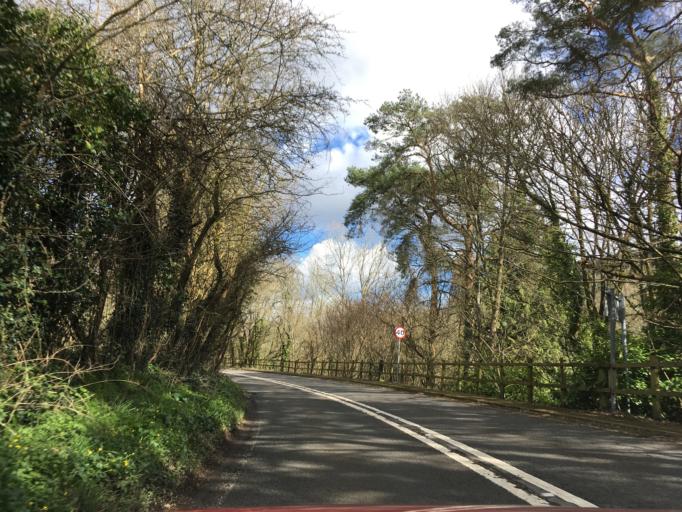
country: GB
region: Wales
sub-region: Monmouthshire
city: Tintern
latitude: 51.7031
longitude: -2.6715
